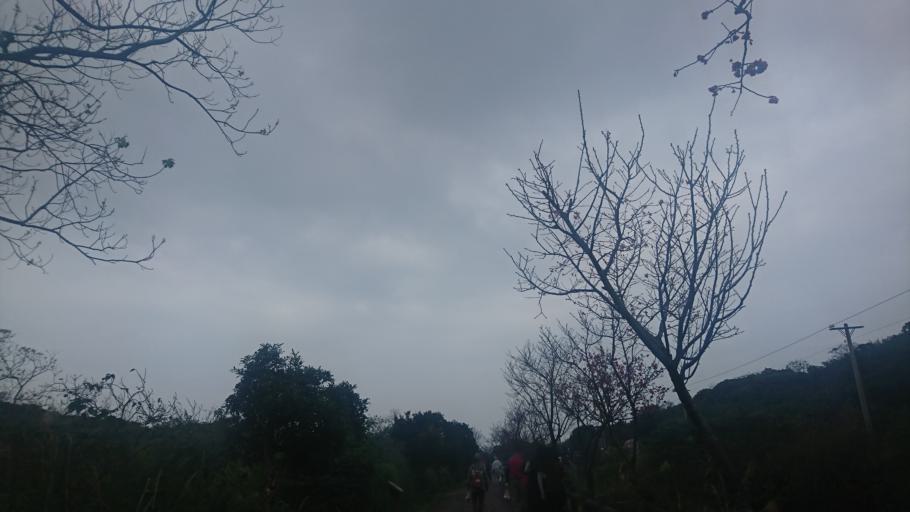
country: TW
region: Taipei
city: Taipei
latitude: 25.2652
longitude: 121.5135
